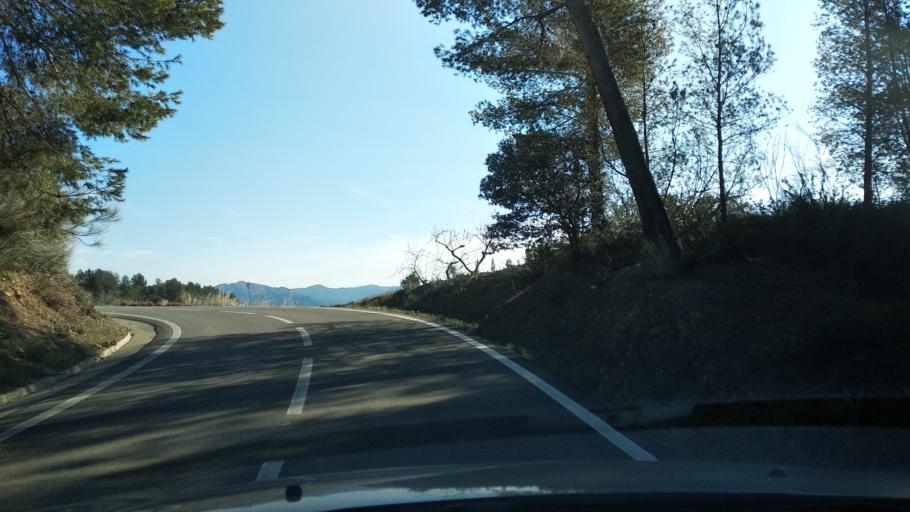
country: ES
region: Catalonia
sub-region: Provincia de Tarragona
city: el Masroig
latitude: 41.1723
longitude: 0.7167
